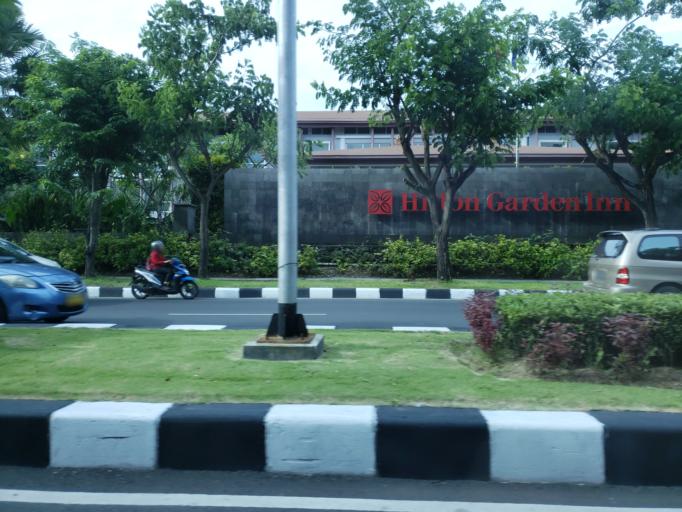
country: ID
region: Bali
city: Kelanabian
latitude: -8.7440
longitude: 115.1711
